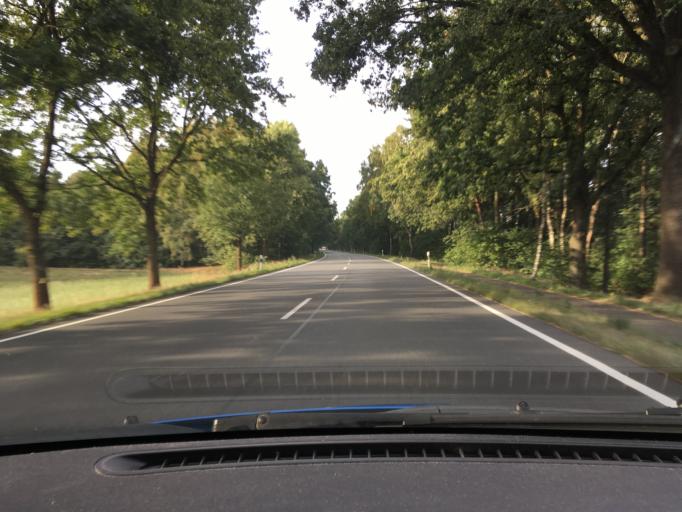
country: DE
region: Lower Saxony
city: Wietzendorf
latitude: 52.9029
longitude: 9.9189
